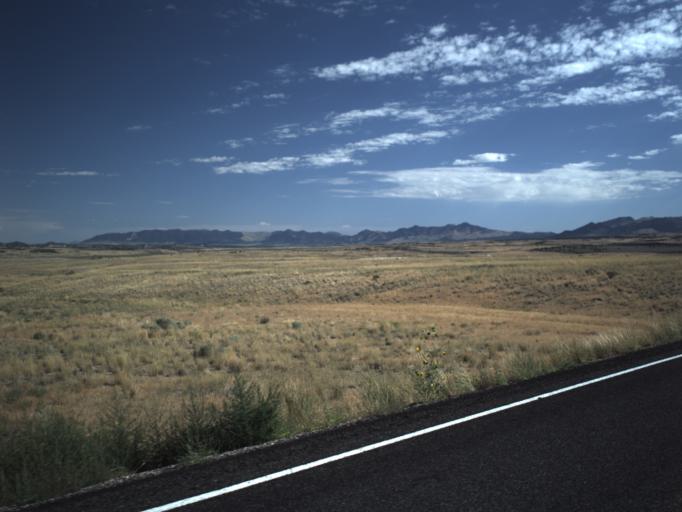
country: US
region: Utah
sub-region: Juab County
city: Mona
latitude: 39.7001
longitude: -112.2208
